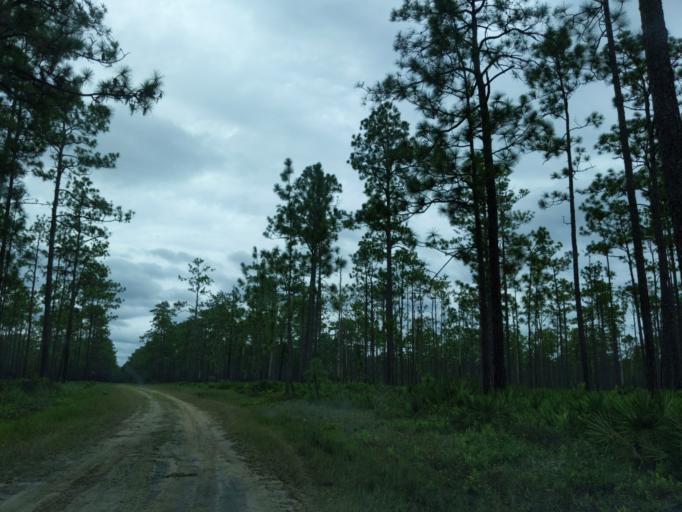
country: US
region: Florida
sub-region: Gadsden County
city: Midway
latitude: 30.3778
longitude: -84.4878
